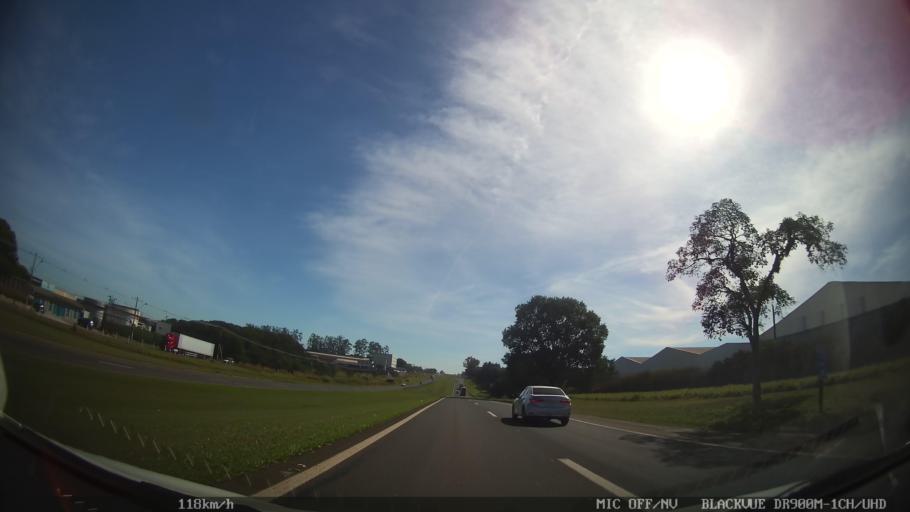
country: BR
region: Sao Paulo
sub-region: Leme
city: Leme
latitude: -22.2110
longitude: -47.3939
